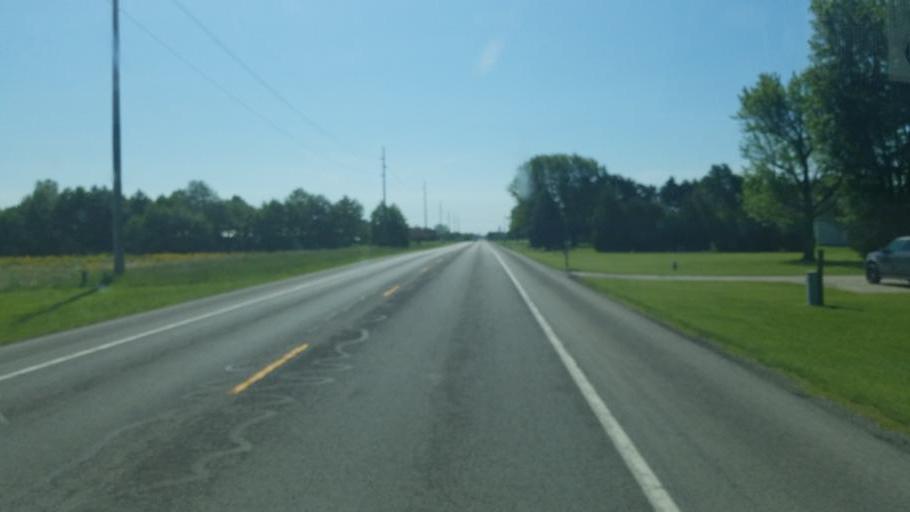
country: US
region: Ohio
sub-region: Hardin County
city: Kenton
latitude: 40.6588
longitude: -83.6413
